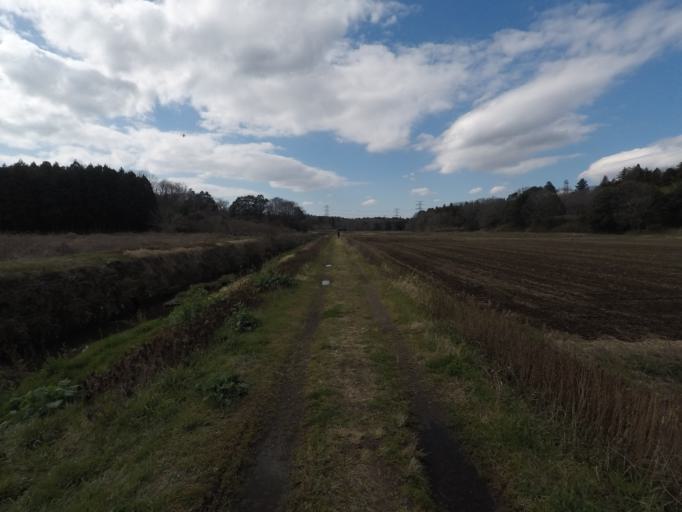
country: JP
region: Ibaraki
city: Ushiku
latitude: 35.9974
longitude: 140.1152
